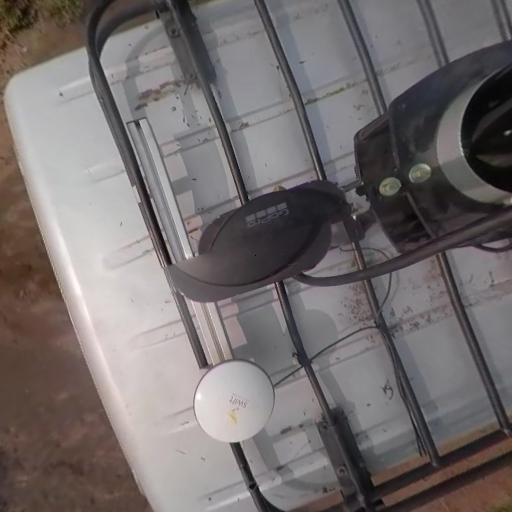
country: IN
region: Telangana
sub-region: Nalgonda
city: Suriapet
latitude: 17.2098
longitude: 79.5075
